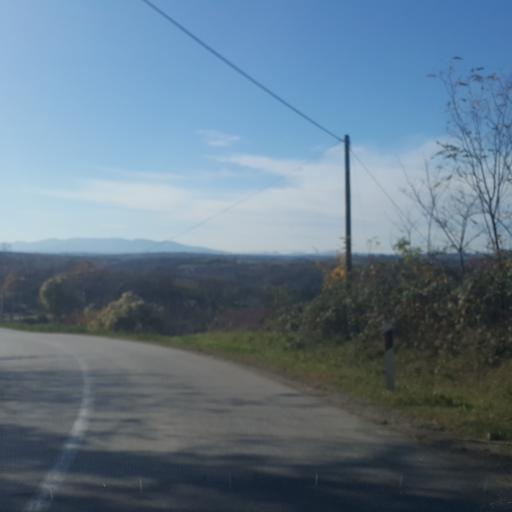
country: RS
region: Central Serbia
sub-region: Sumadijski Okrug
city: Raca
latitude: 44.2392
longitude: 20.8396
